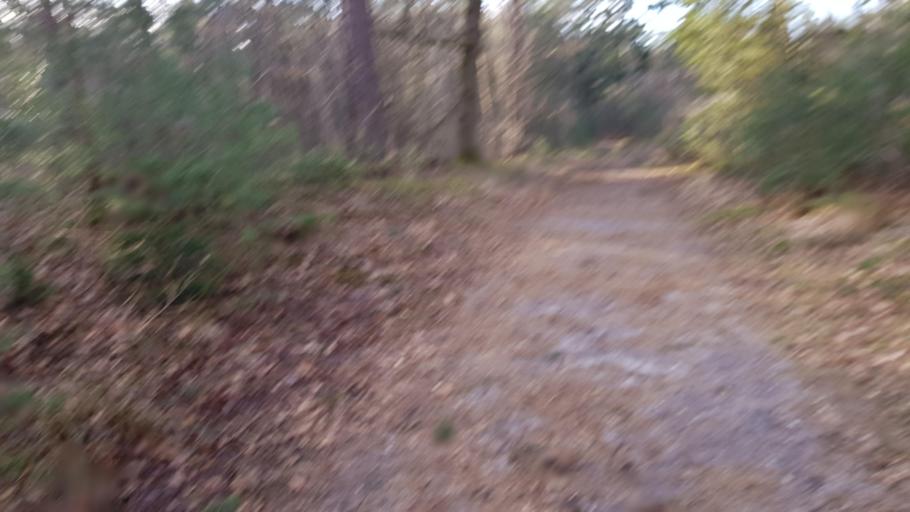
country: NL
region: North Holland
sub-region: Gemeente Hilversum
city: Hilversum
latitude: 52.1779
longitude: 5.2085
